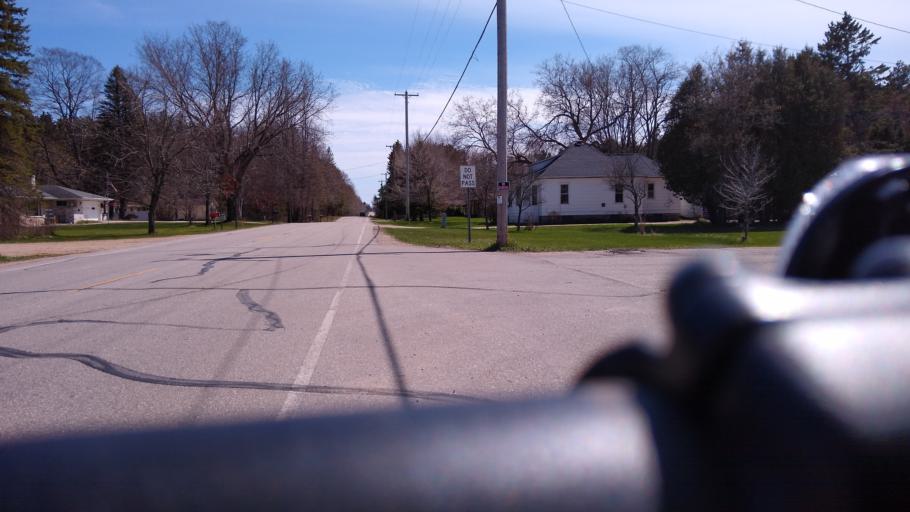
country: US
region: Michigan
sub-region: Delta County
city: Escanaba
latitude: 45.7325
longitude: -87.2025
